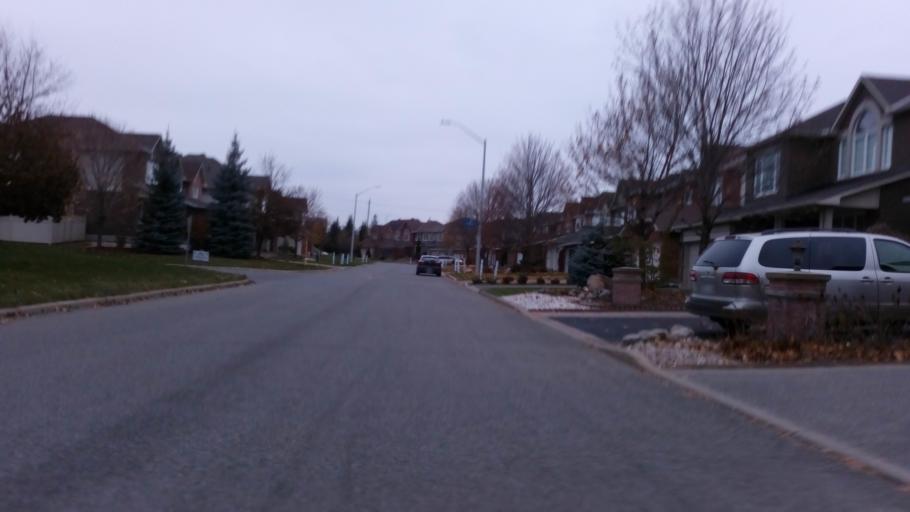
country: CA
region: Ontario
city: Ottawa
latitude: 45.3549
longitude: -75.6368
